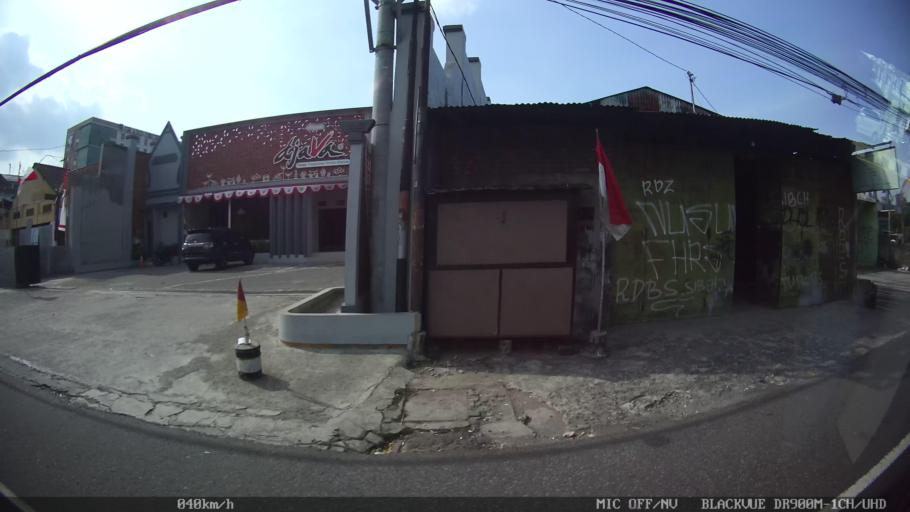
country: ID
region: Daerah Istimewa Yogyakarta
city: Depok
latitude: -7.7831
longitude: 110.4252
